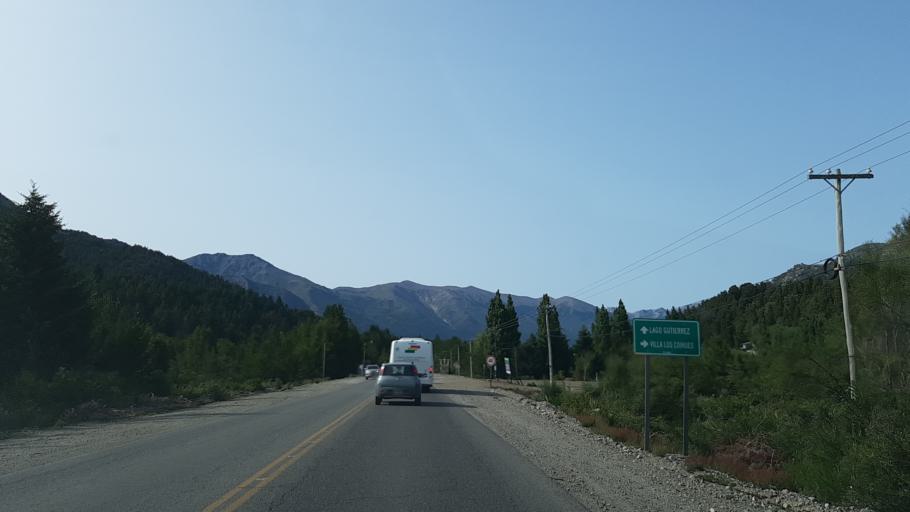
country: AR
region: Rio Negro
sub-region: Departamento de Bariloche
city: San Carlos de Bariloche
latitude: -41.1431
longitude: -71.4106
